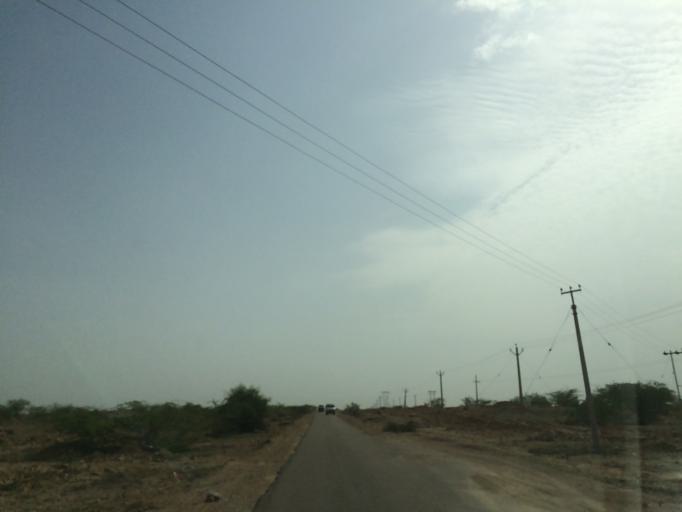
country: IN
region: Rajasthan
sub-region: Jaisalmer
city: Jaisalmer
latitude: 26.8983
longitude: 70.9272
